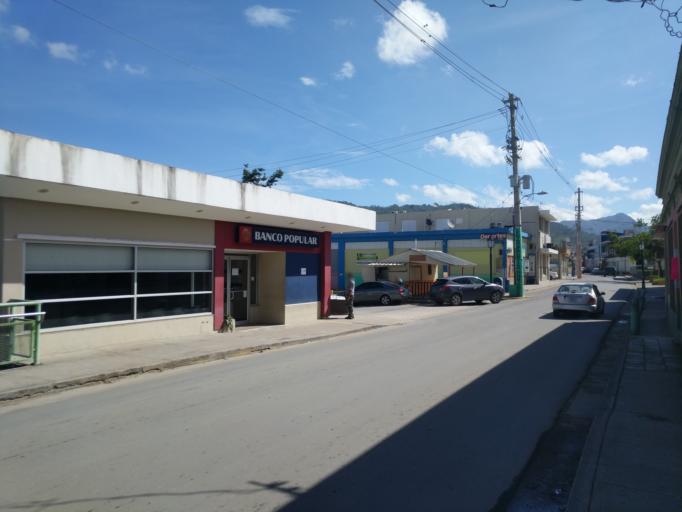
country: PR
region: Utuado
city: Utuado
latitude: 18.2660
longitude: -66.7039
